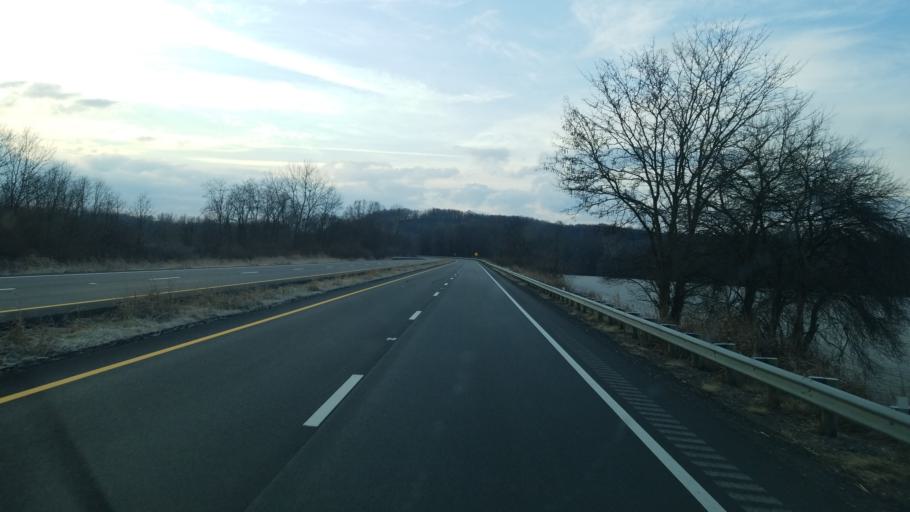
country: US
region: Ohio
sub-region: Ross County
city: Chillicothe
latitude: 39.3132
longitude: -82.9613
